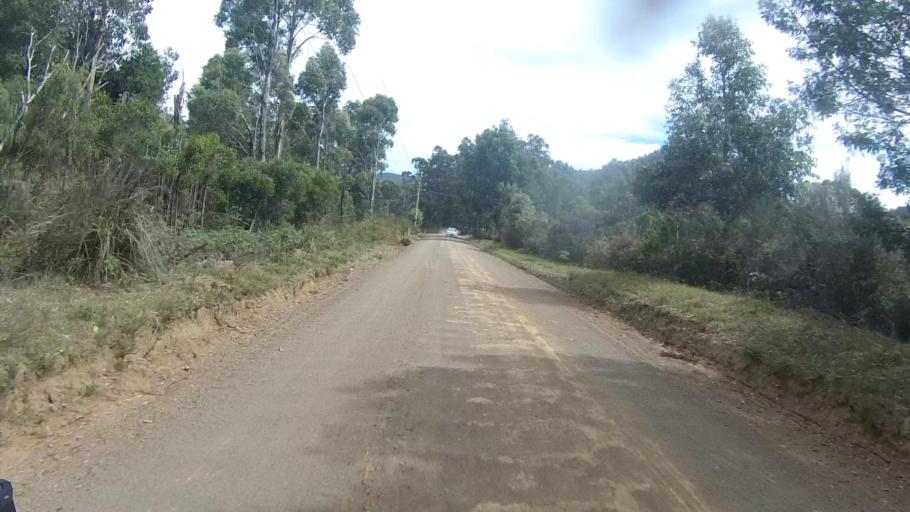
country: AU
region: Tasmania
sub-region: Sorell
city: Sorell
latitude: -42.7711
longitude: 147.8078
